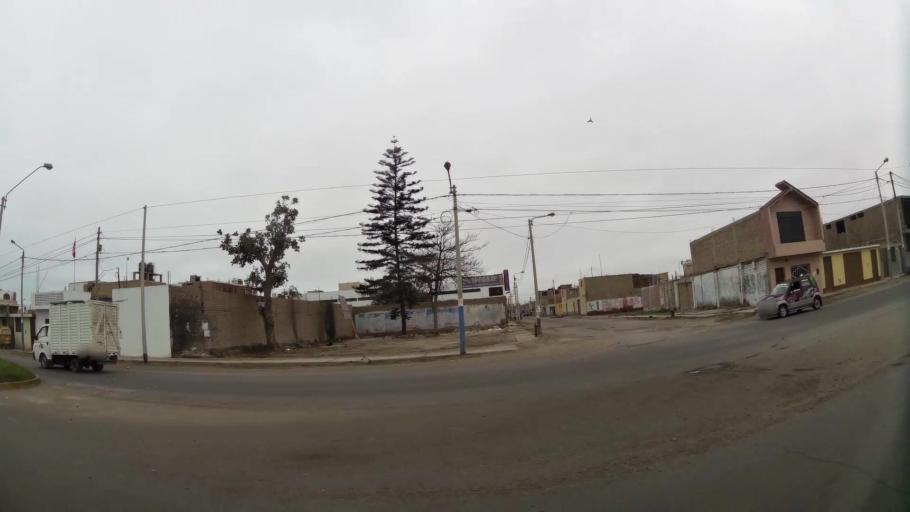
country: PE
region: Ica
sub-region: Provincia de Pisco
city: Pisco
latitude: -13.7164
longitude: -76.2176
